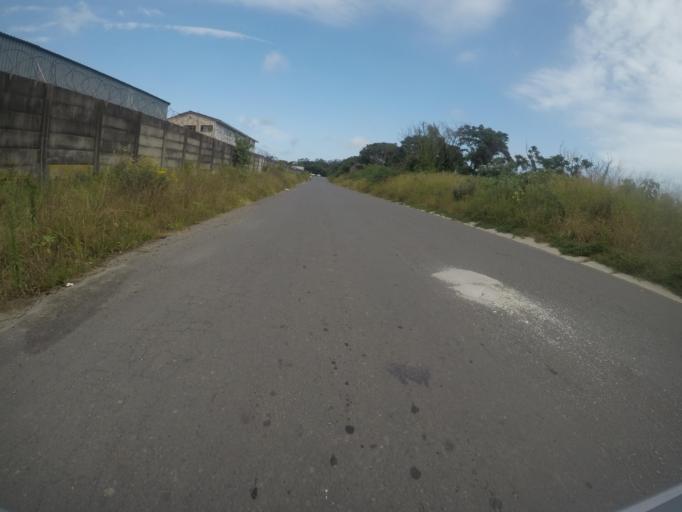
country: ZA
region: Eastern Cape
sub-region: Buffalo City Metropolitan Municipality
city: East London
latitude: -32.9891
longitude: 27.8875
